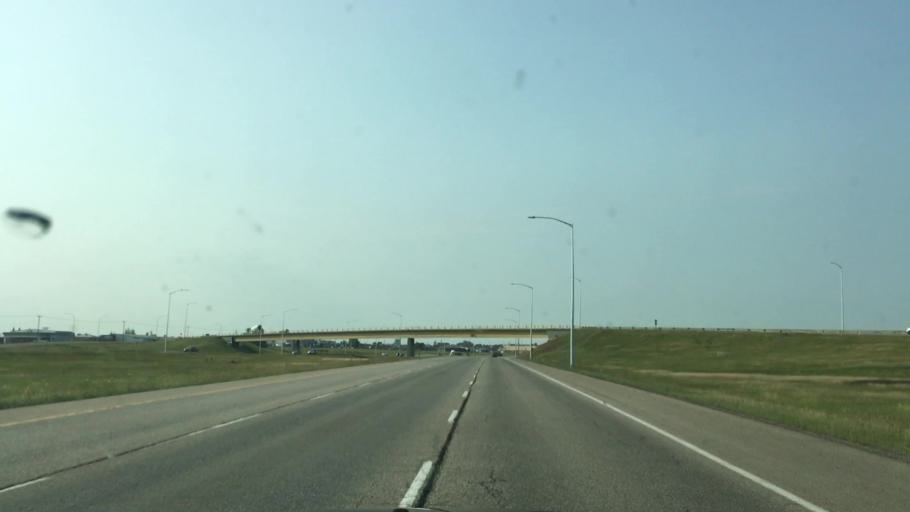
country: CA
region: Alberta
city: Leduc
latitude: 53.2869
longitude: -113.5499
